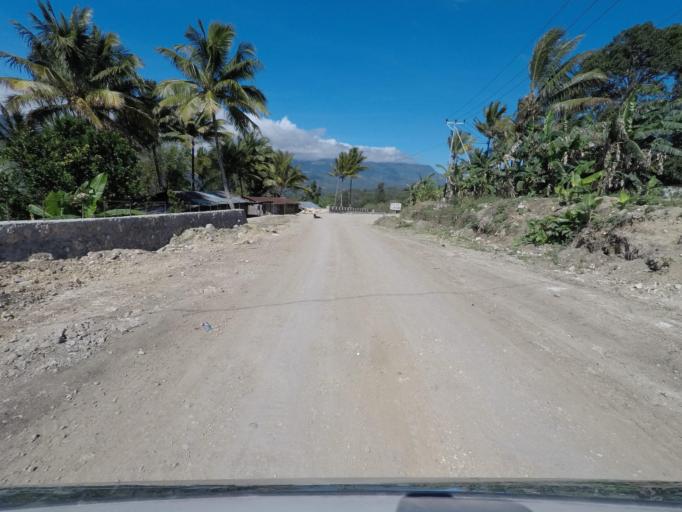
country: TL
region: Baucau
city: Venilale
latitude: -8.6449
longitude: 126.3754
